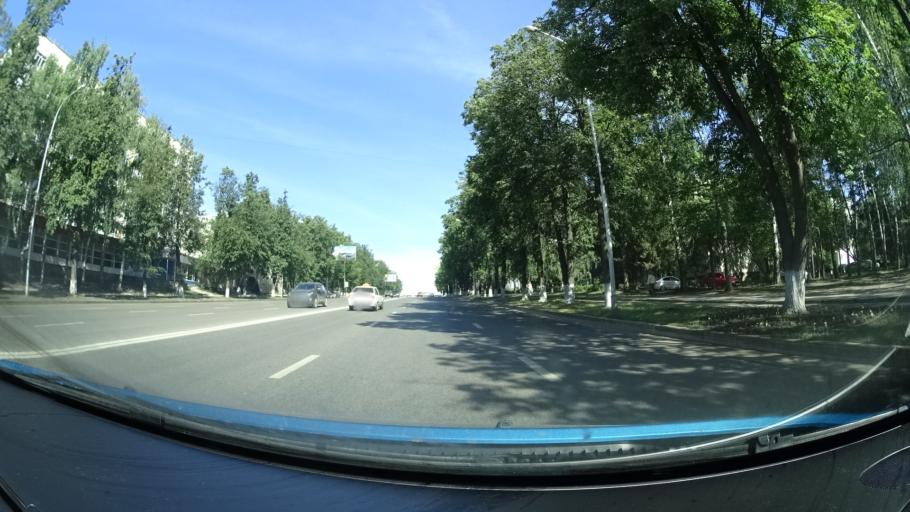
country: RU
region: Bashkortostan
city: Ufa
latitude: 54.7575
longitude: 56.0018
